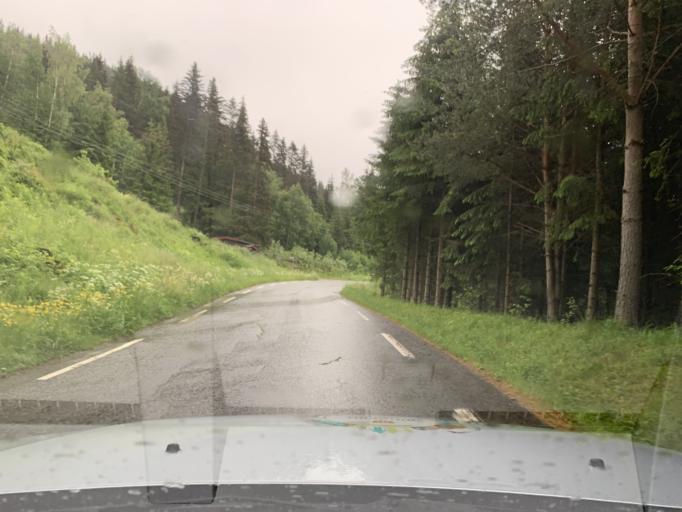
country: NO
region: Oppland
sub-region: Oyer
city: Tretten
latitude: 61.3947
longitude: 10.2391
